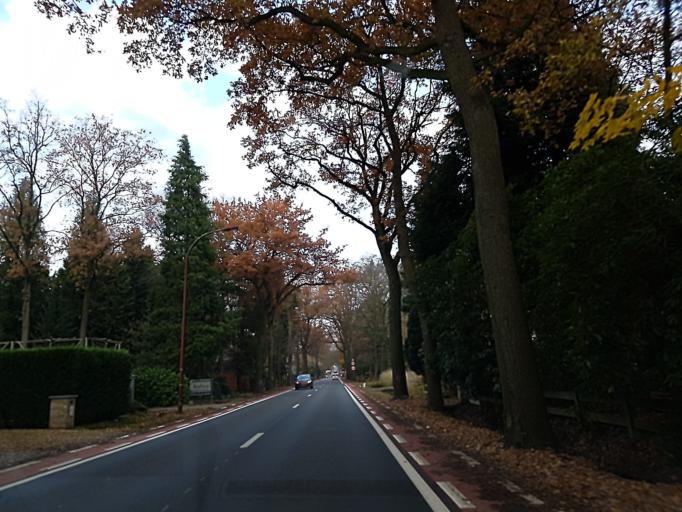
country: BE
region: Flanders
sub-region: Provincie Antwerpen
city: Kalmthout
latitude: 51.3673
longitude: 4.4679
